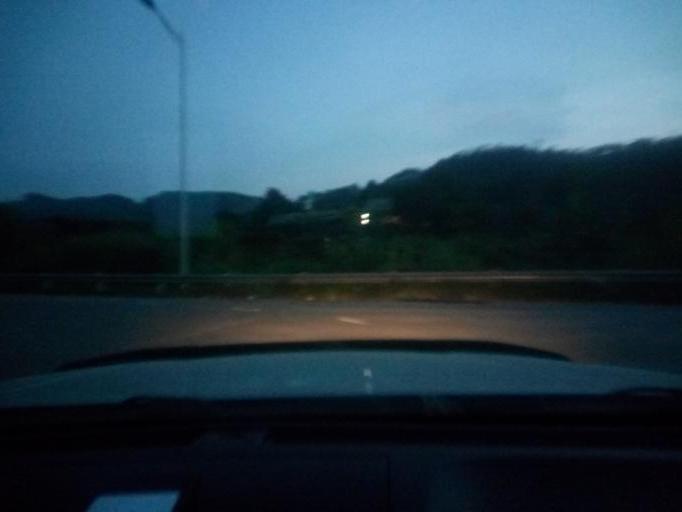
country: VN
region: Yen Bai
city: Co Phuc
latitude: 21.8773
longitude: 104.6742
